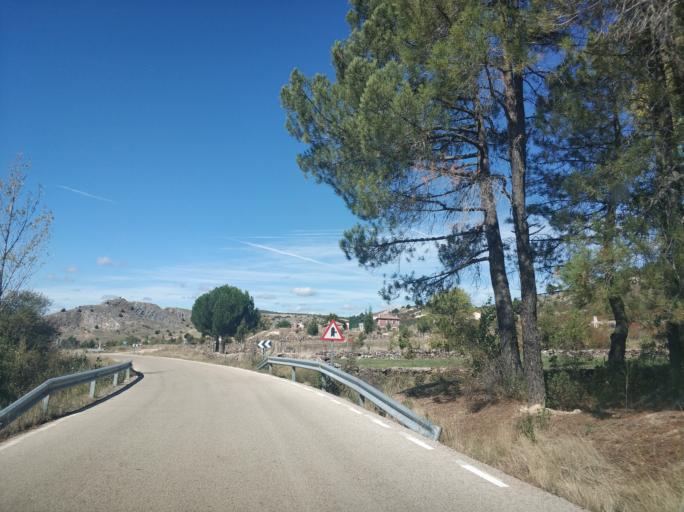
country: ES
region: Castille and Leon
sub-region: Provincia de Soria
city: Espeja de San Marcelino
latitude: 41.7993
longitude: -3.2170
